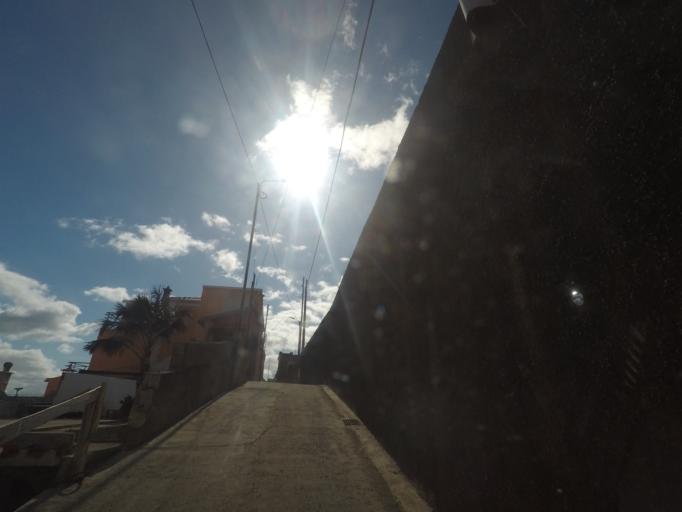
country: PT
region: Madeira
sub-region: Camara de Lobos
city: Curral das Freiras
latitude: 32.6809
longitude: -16.9459
